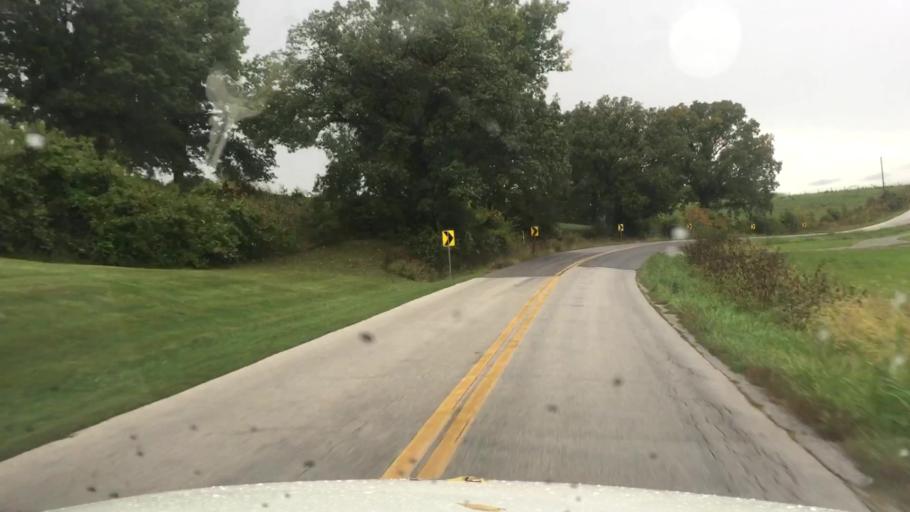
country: US
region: Missouri
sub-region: Boone County
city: Columbia
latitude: 38.9242
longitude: -92.4684
